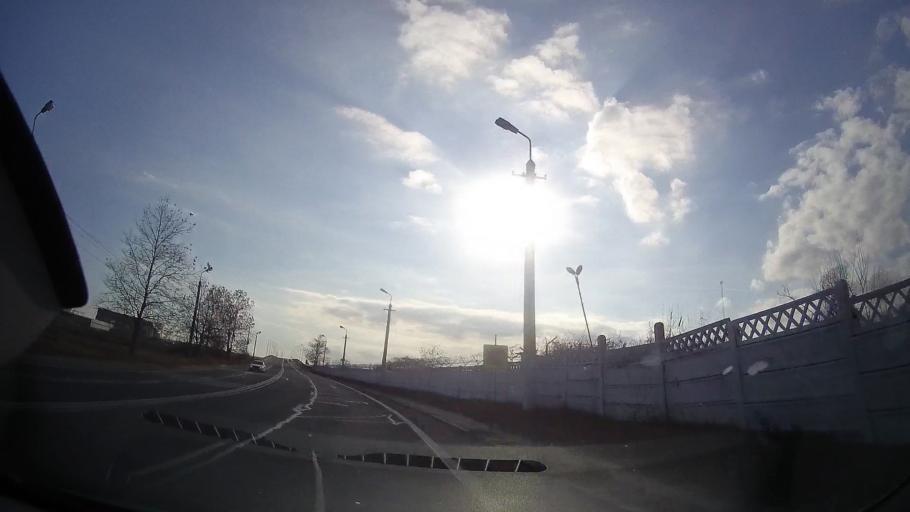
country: RO
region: Constanta
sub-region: Municipiul Mangalia
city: Mangalia
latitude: 43.8076
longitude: 28.5615
